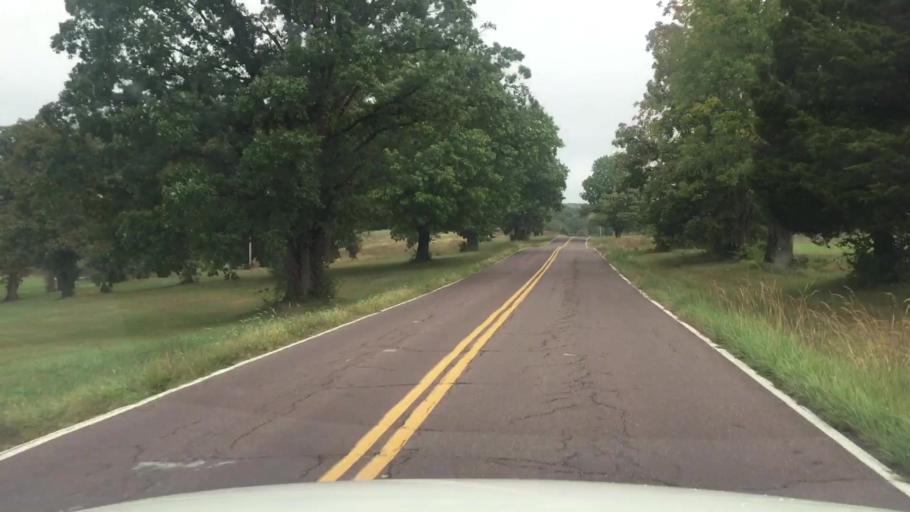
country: US
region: Missouri
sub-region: Boone County
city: Columbia
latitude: 38.8507
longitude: -92.3336
